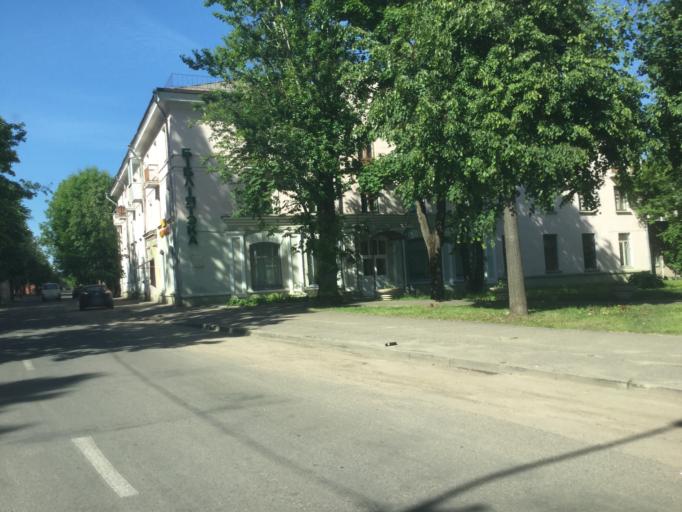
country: BY
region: Vitebsk
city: Vitebsk
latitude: 55.1893
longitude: 30.1907
